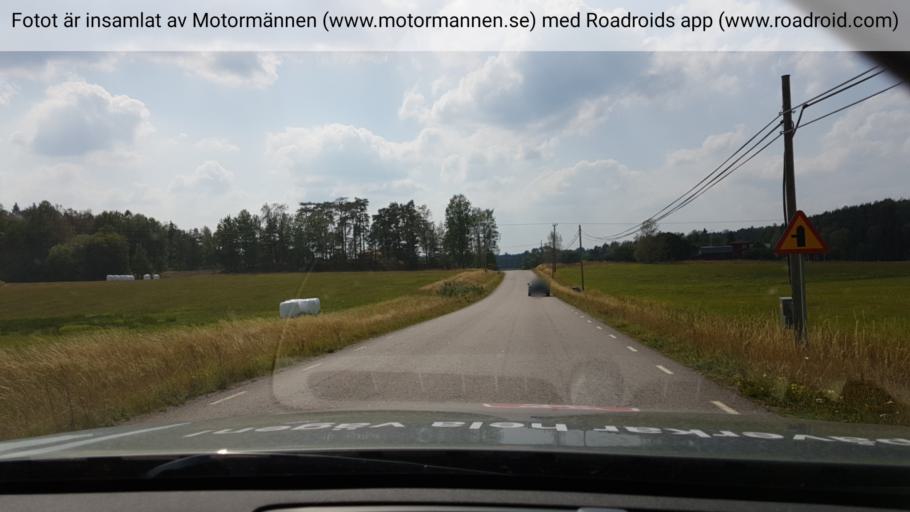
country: SE
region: Soedermanland
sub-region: Gnesta Kommun
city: Gnesta
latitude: 59.0437
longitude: 17.2709
